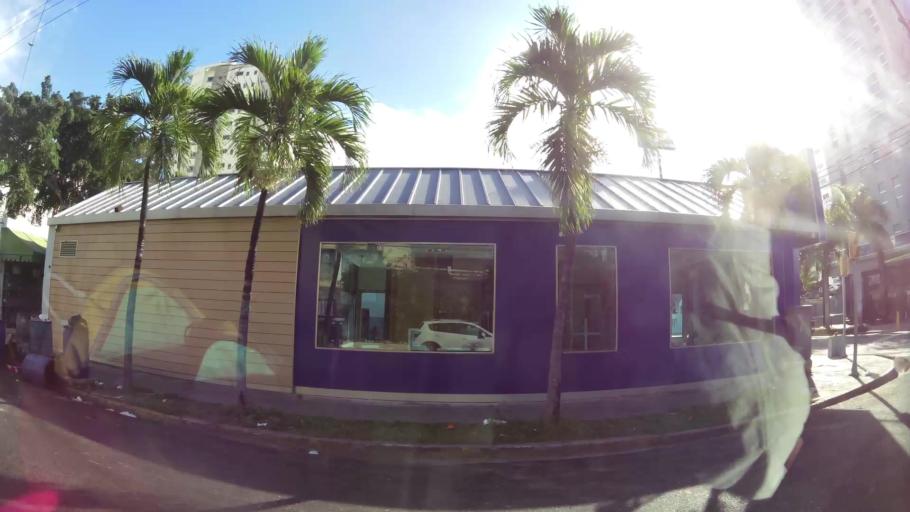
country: DO
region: Nacional
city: La Julia
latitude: 18.4673
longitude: -69.9362
